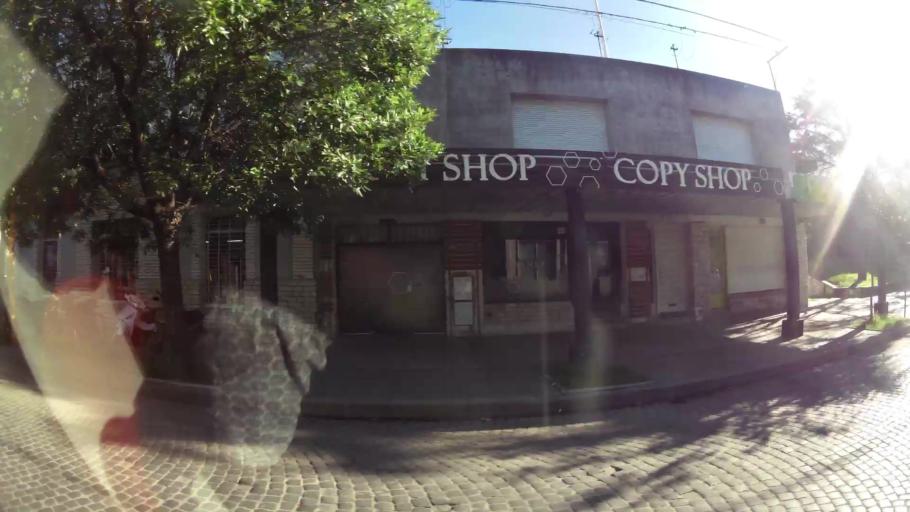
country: AR
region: Cordoba
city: San Francisco
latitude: -31.4315
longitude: -62.0823
